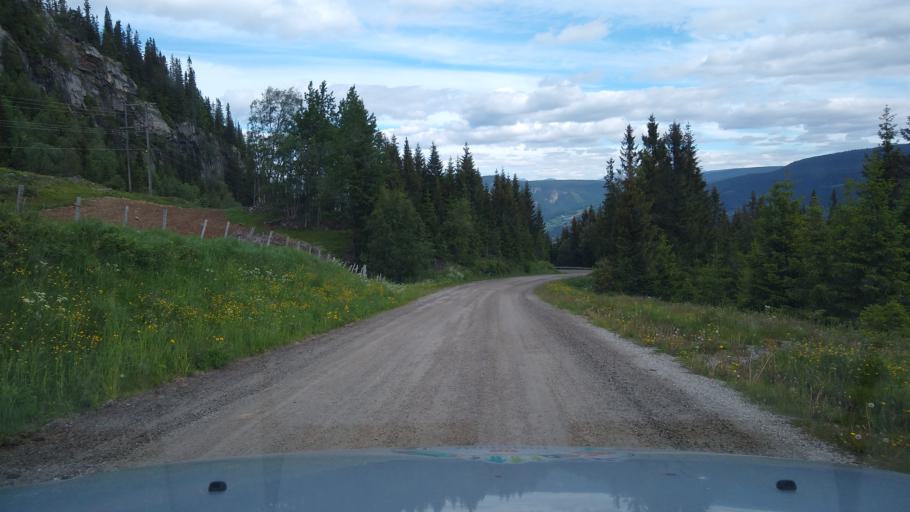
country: NO
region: Oppland
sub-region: Ringebu
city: Ringebu
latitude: 61.4947
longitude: 10.1452
